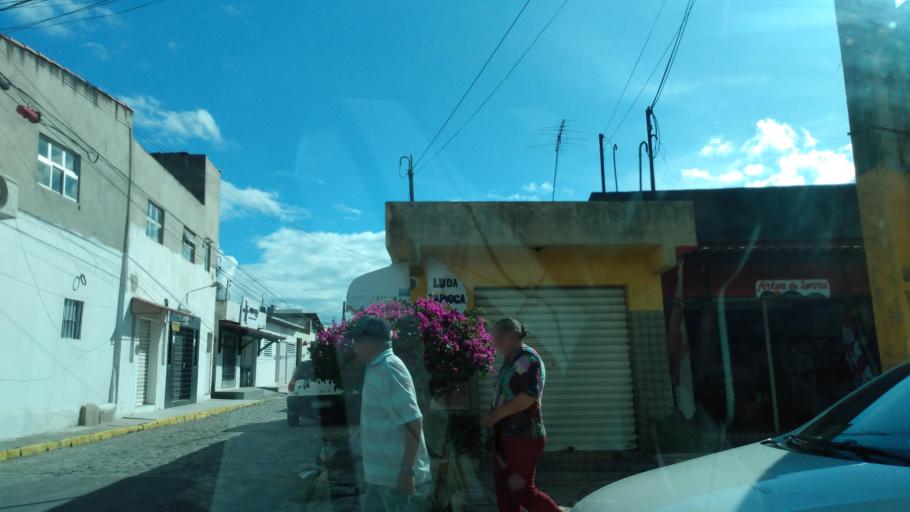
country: ET
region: Oromiya
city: Gore
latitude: 8.1962
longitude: 35.5609
